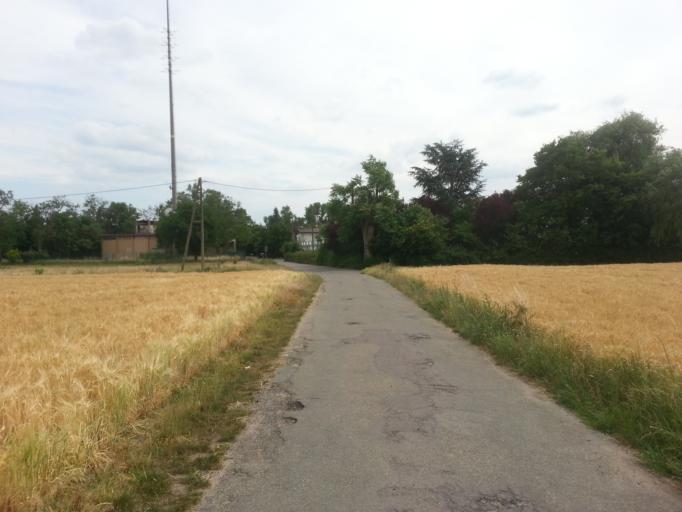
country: DE
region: Baden-Wuerttemberg
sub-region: Karlsruhe Region
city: Mannheim
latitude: 49.5257
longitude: 8.5209
